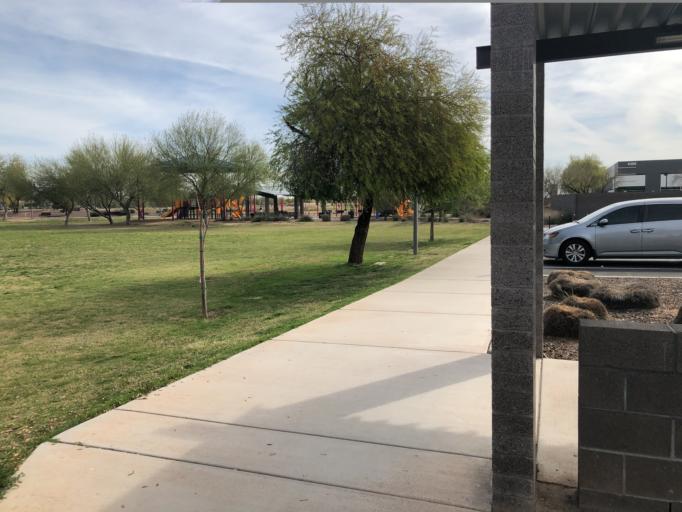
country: US
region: Arizona
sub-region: Maricopa County
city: Guadalupe
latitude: 33.3080
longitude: -111.9196
